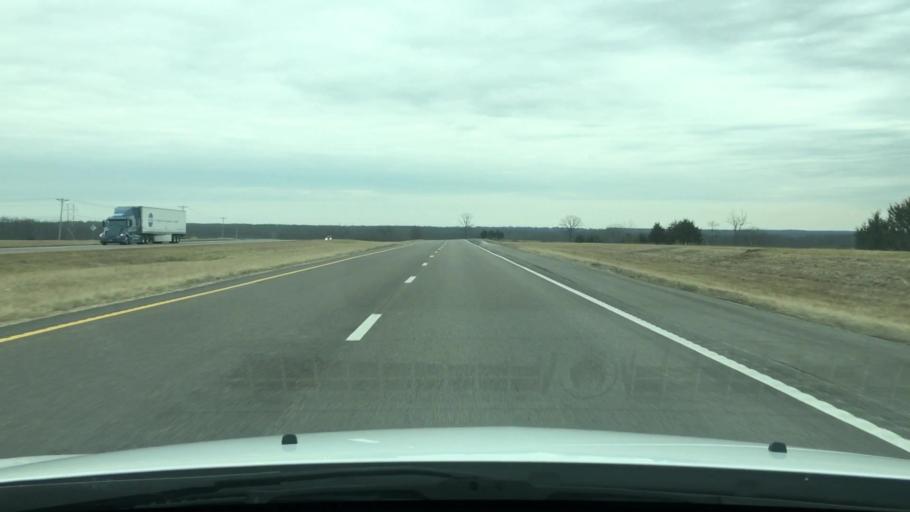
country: US
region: Missouri
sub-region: Callaway County
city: Fulton
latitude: 38.9655
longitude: -91.9071
